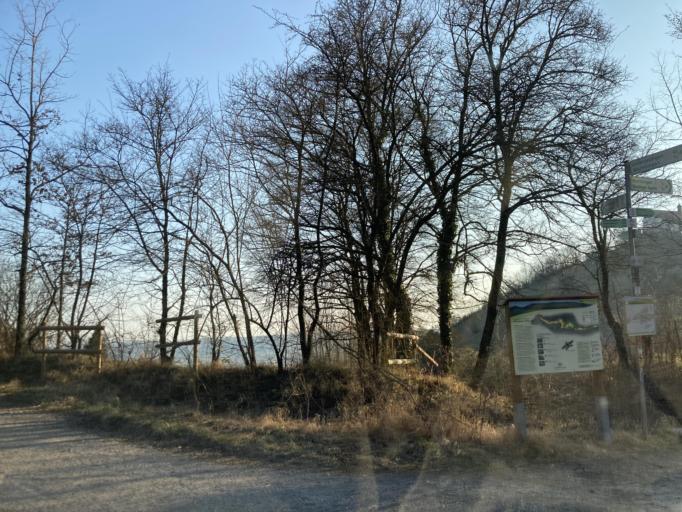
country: DE
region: Baden-Wuerttemberg
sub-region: Tuebingen Region
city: Rottenburg
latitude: 48.5082
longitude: 8.9861
